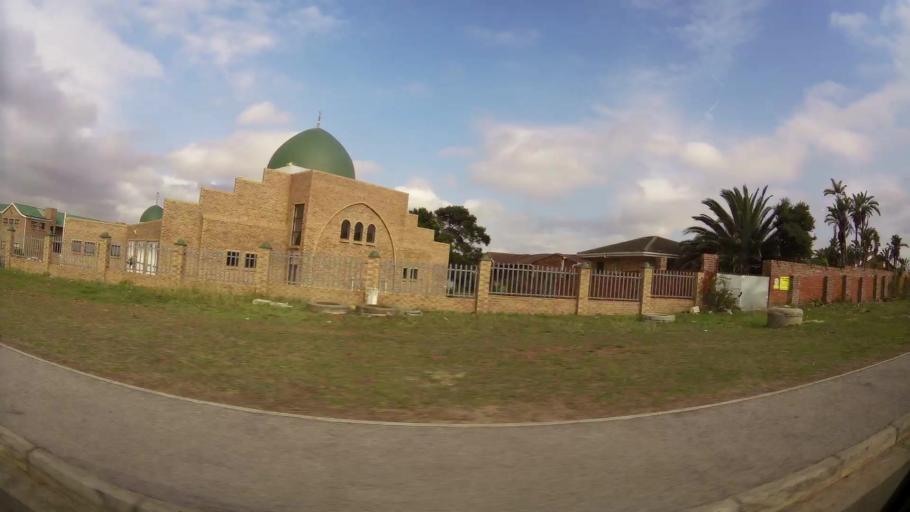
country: ZA
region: Eastern Cape
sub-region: Nelson Mandela Bay Metropolitan Municipality
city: Port Elizabeth
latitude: -33.9193
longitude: 25.5300
